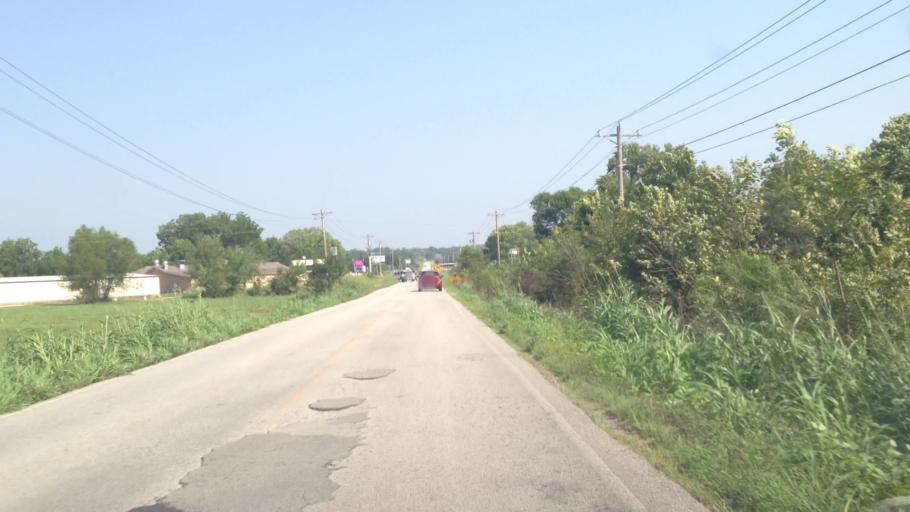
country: US
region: Oklahoma
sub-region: Delaware County
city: Cleora
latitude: 36.5700
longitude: -94.9707
